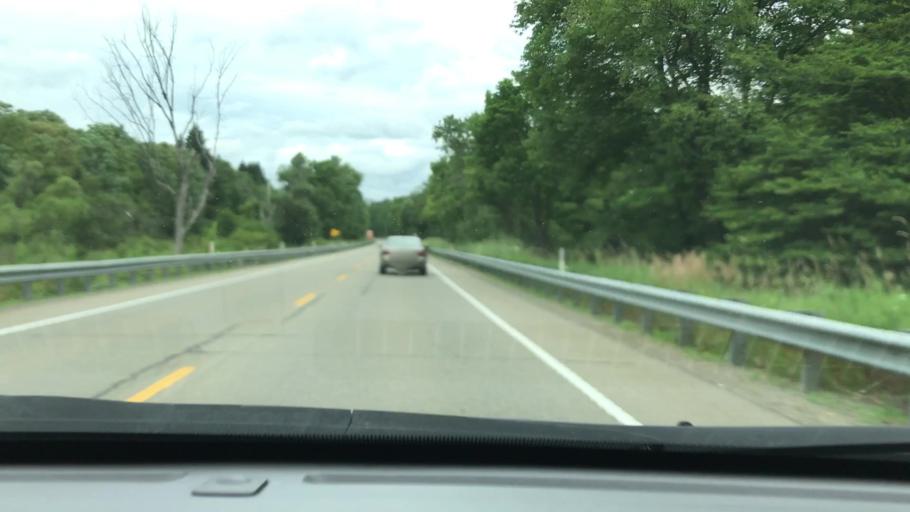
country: US
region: Pennsylvania
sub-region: Elk County
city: Johnsonburg
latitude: 41.5085
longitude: -78.6792
